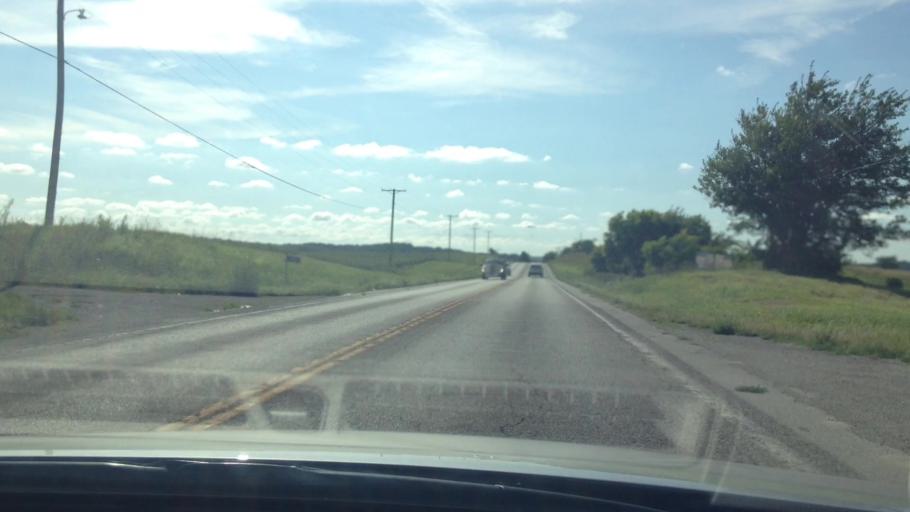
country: US
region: Missouri
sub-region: Platte County
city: Platte City
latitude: 39.3679
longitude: -94.8377
